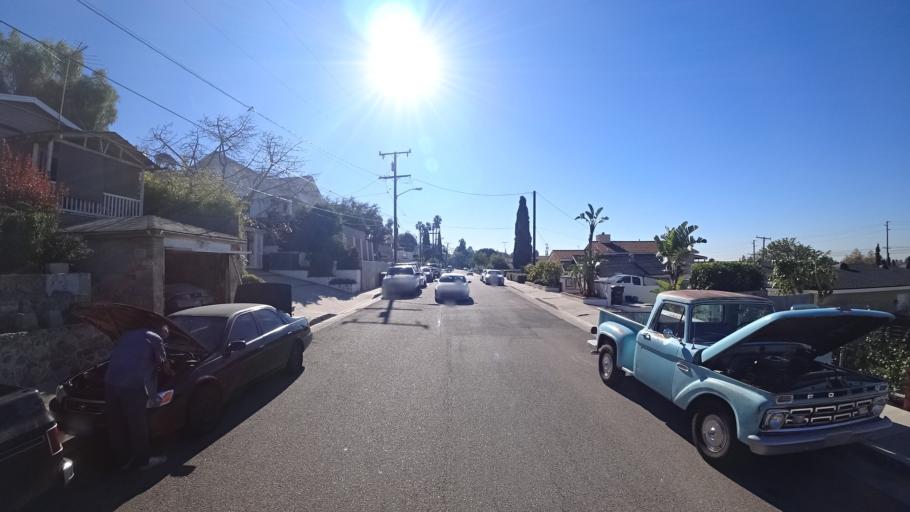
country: US
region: California
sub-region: Orange County
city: North Tustin
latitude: 33.7816
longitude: -117.8038
